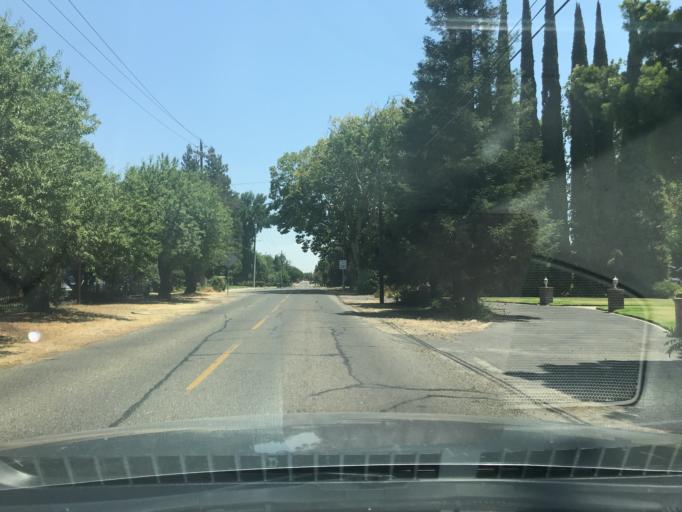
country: US
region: California
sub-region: Merced County
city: Atwater
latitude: 37.3641
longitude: -120.6067
